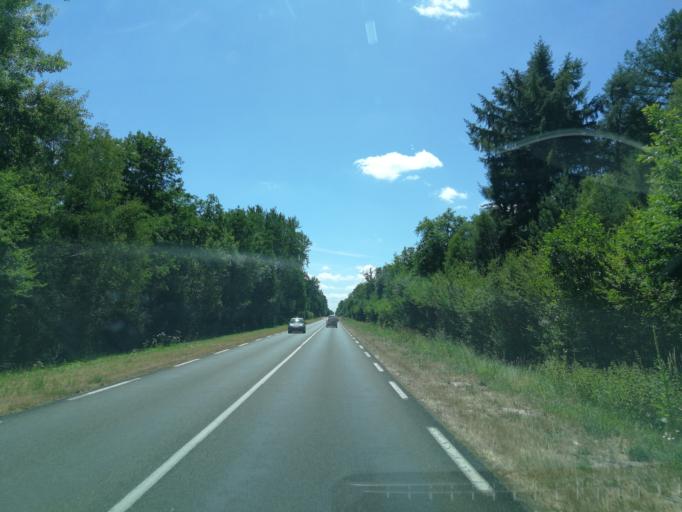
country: FR
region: Centre
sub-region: Departement du Loiret
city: La Ferte-Saint-Aubin
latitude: 47.6770
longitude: 1.9674
